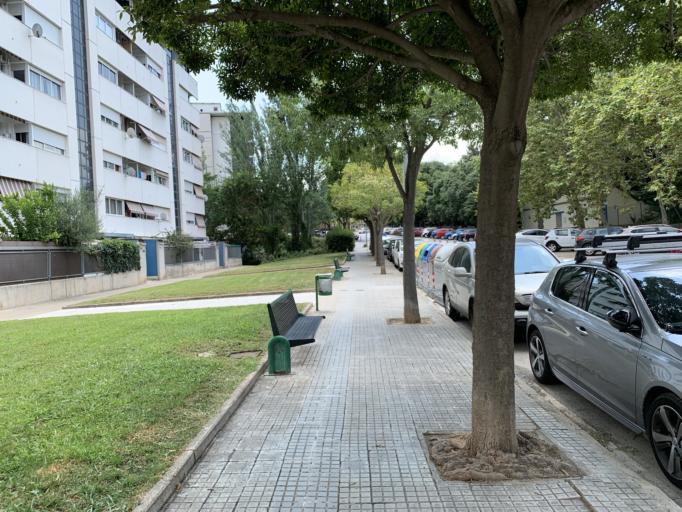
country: ES
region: Catalonia
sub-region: Provincia de Barcelona
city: Cerdanyola del Valles
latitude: 41.4975
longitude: 2.1294
